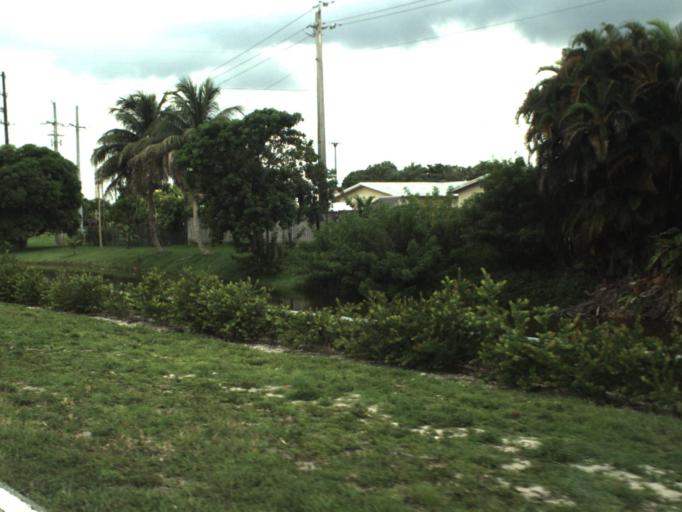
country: US
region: Florida
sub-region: Broward County
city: Cooper City
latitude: 26.0304
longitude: -80.2674
